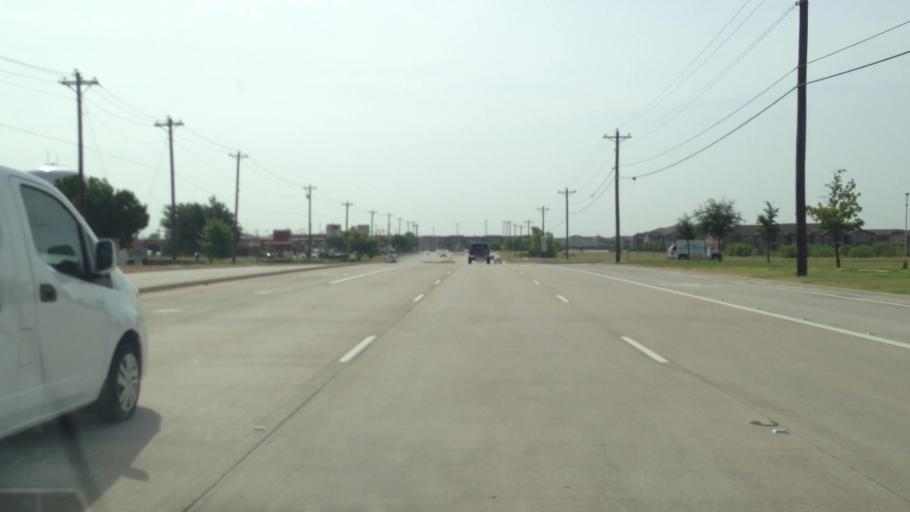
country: US
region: Texas
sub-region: Denton County
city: Lewisville
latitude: 33.0083
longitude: -97.0244
